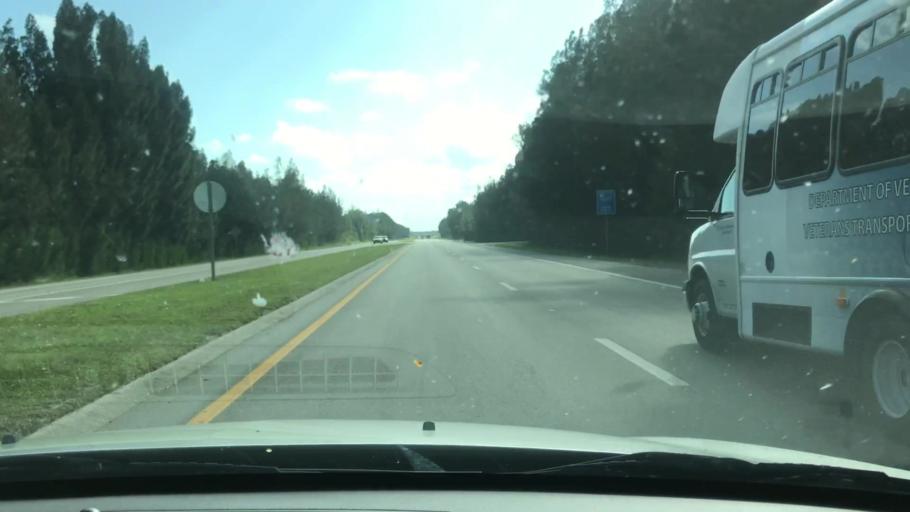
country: US
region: Florida
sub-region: Charlotte County
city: Charlotte Park
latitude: 26.8584
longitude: -81.9864
